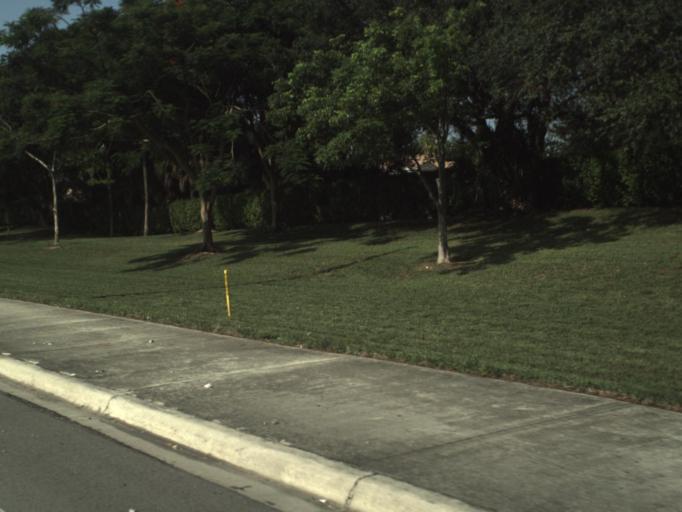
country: US
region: Florida
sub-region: Broward County
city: Parkland
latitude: 26.3095
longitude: -80.2023
